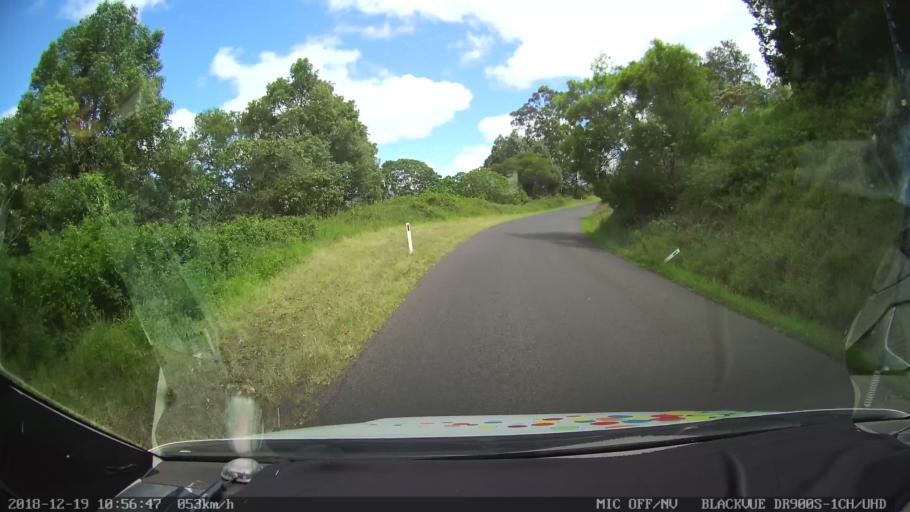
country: AU
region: New South Wales
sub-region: Lismore Municipality
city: Nimbin
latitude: -28.5922
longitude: 153.2611
